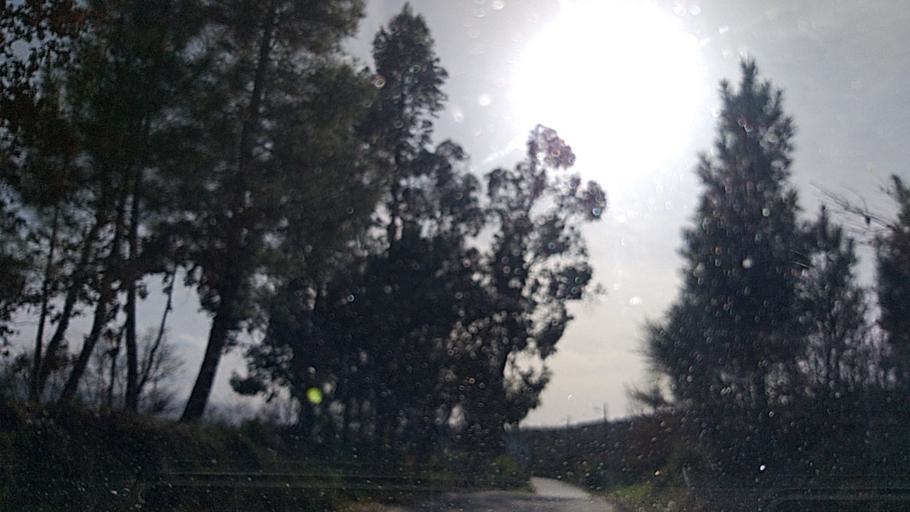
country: PT
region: Guarda
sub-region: Celorico da Beira
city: Celorico da Beira
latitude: 40.6484
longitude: -7.4271
